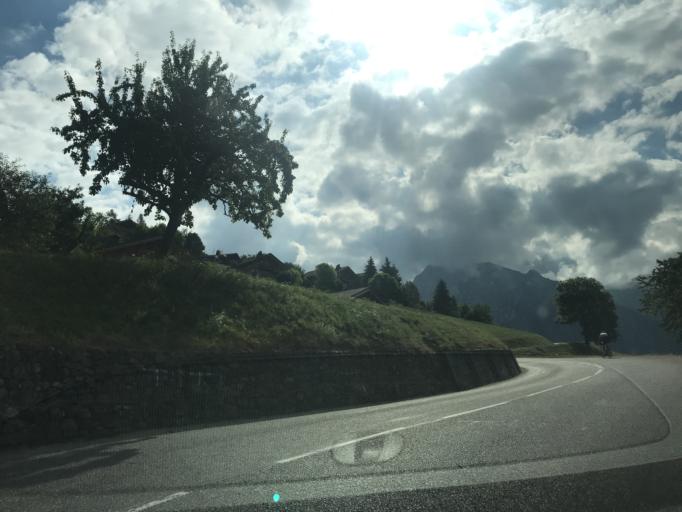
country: FR
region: Rhone-Alpes
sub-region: Departement de la Haute-Savoie
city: Thones
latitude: 45.8628
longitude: 6.3712
